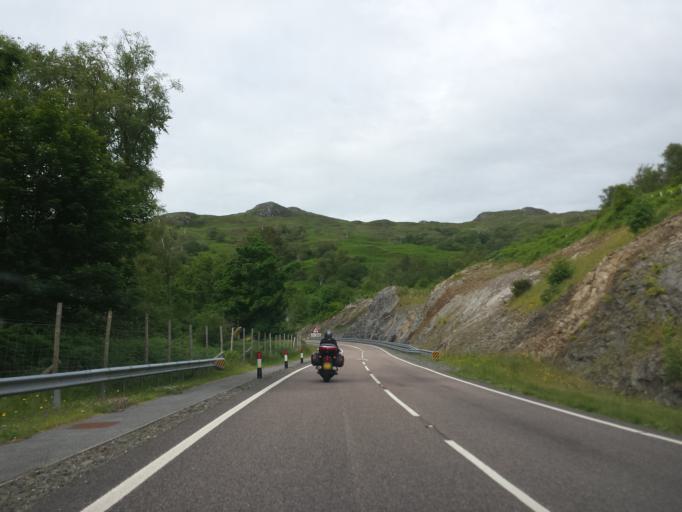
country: GB
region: Scotland
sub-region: Argyll and Bute
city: Isle Of Mull
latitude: 56.9097
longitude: -5.8225
